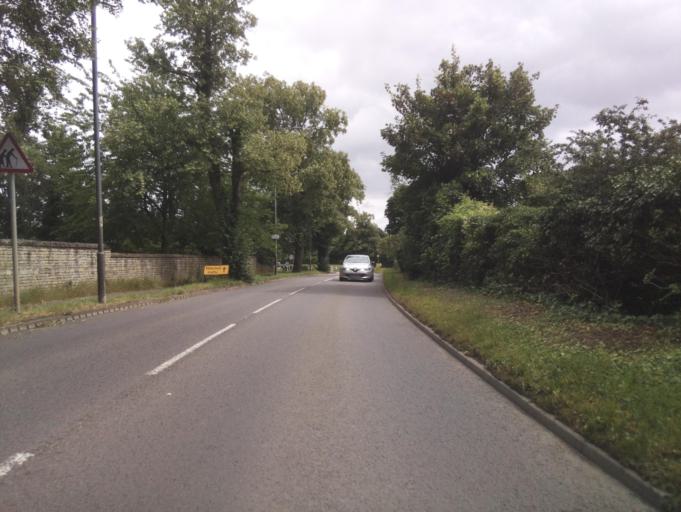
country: GB
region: England
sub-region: Lincolnshire
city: Stamford
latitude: 52.6551
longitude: -0.4662
